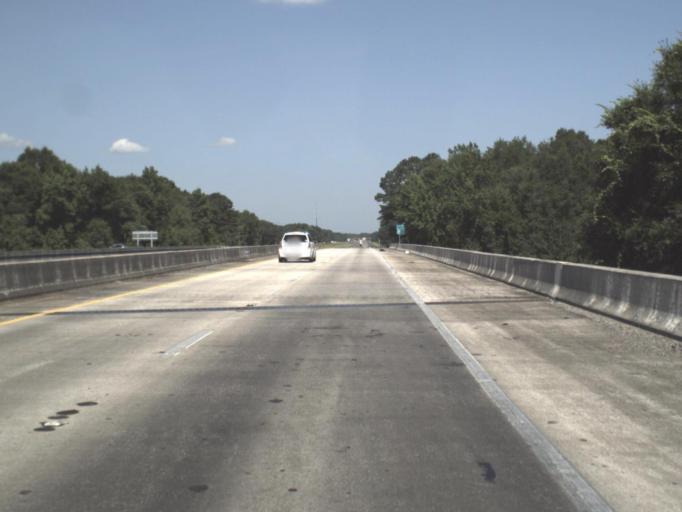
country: US
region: Florida
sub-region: Suwannee County
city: Live Oak
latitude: 30.3579
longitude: -83.1926
